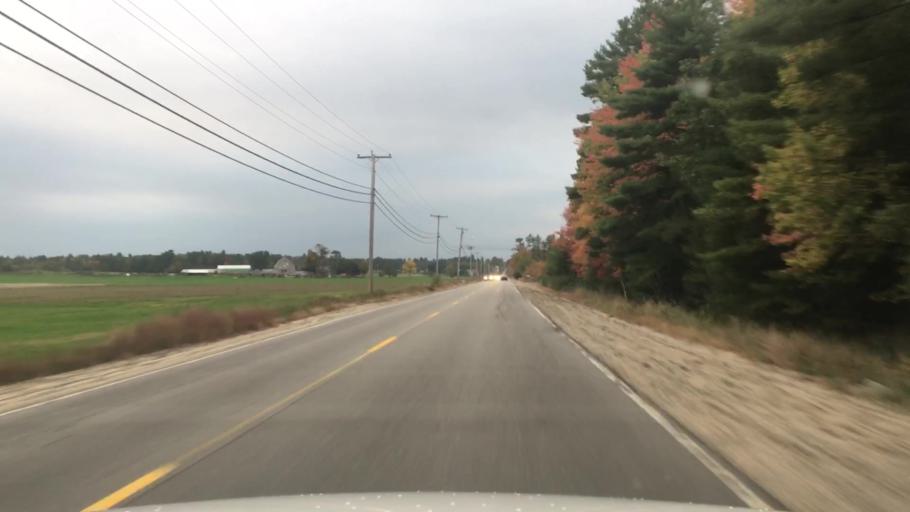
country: US
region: Maine
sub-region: York County
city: Buxton
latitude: 43.6408
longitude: -70.5253
